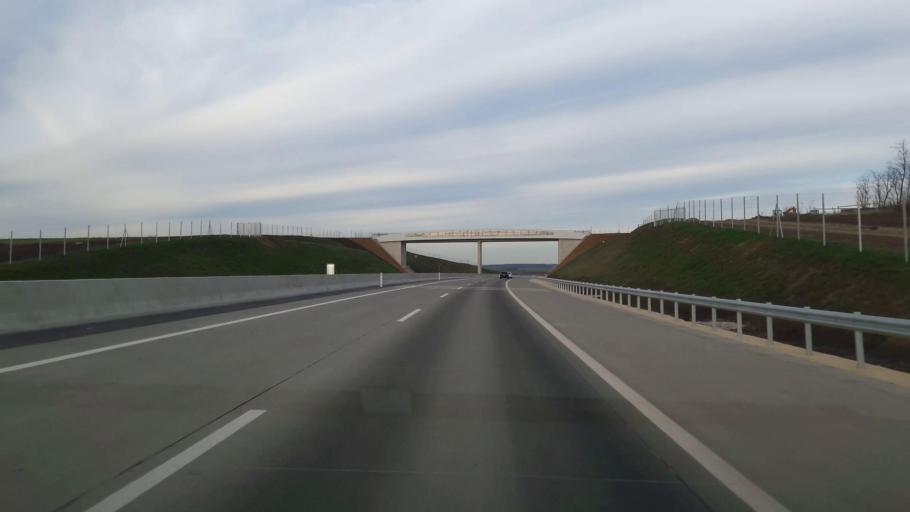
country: AT
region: Lower Austria
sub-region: Politischer Bezirk Mistelbach
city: Grosskrut
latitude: 48.6273
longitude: 16.6765
